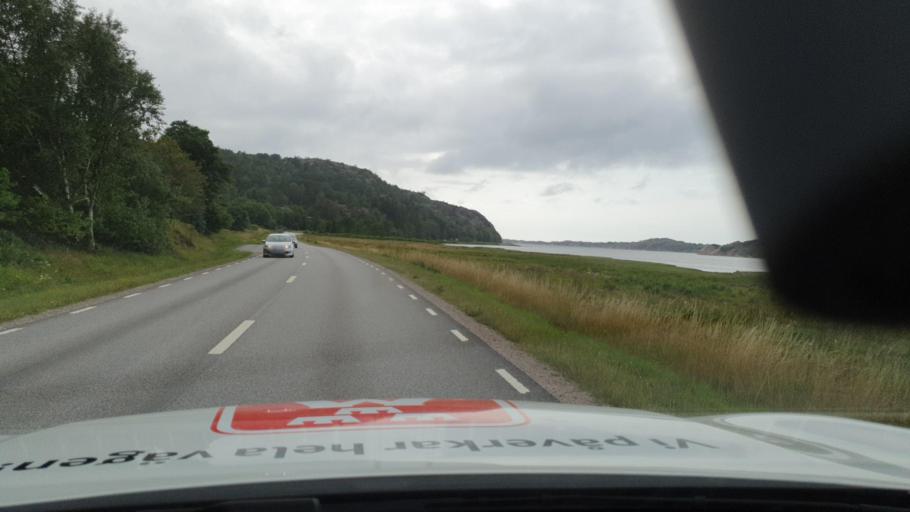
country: SE
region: Vaestra Goetaland
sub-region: Sotenas Kommun
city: Hunnebostrand
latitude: 58.4871
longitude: 11.3612
